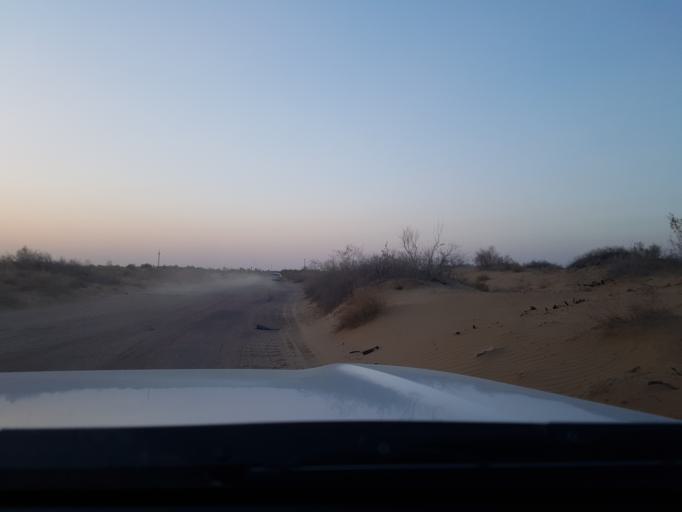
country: UZ
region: Xorazm
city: Khiwa
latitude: 41.2837
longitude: 60.3010
